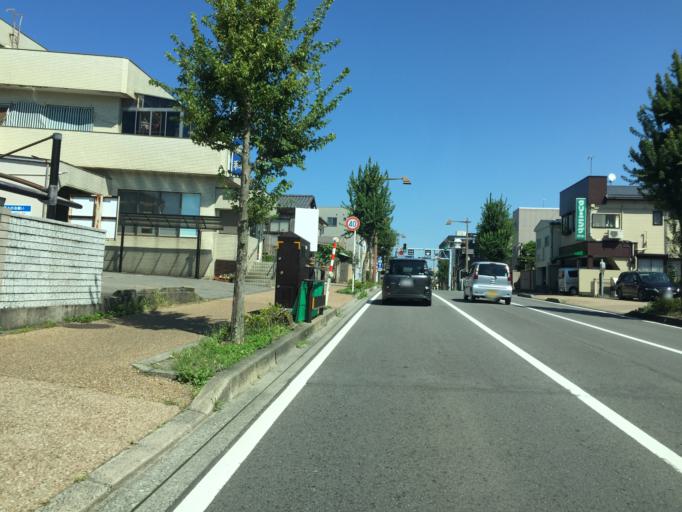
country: JP
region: Niigata
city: Niigata-shi
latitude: 37.9071
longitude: 139.0147
